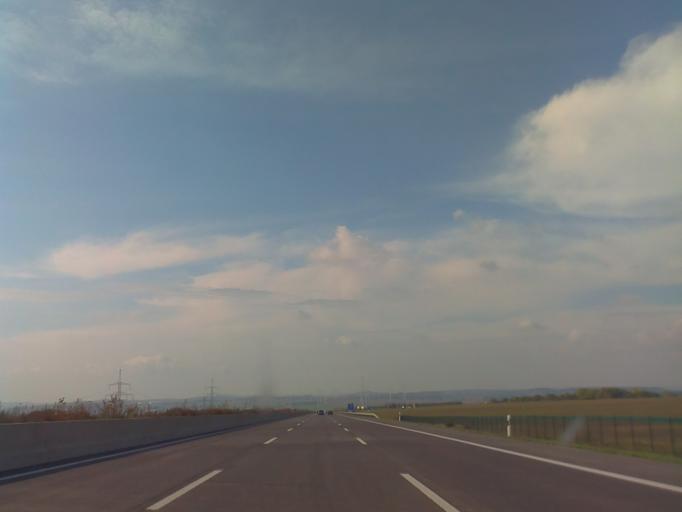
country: DE
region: Thuringia
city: Haina
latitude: 50.9897
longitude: 10.4574
